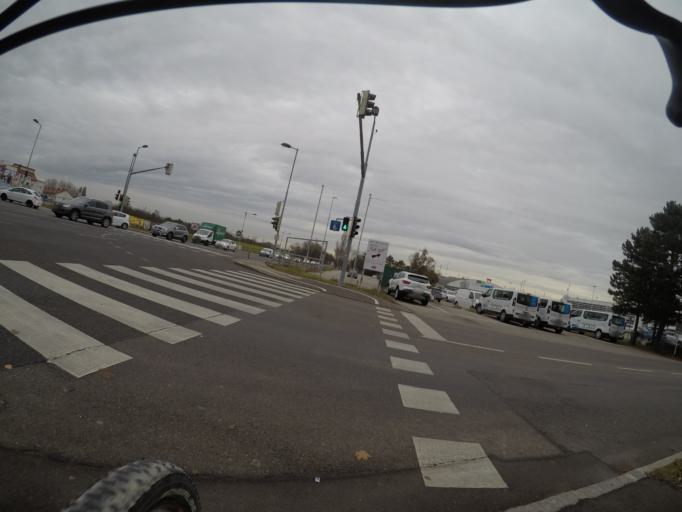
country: AT
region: Lower Austria
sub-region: Politischer Bezirk Modling
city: Wiener Neudorf
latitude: 48.0995
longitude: 16.3107
